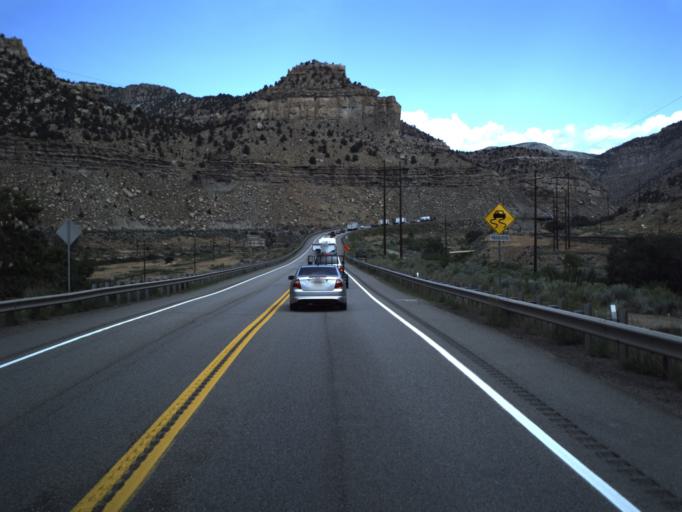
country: US
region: Utah
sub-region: Carbon County
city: Helper
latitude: 39.7032
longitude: -110.8689
